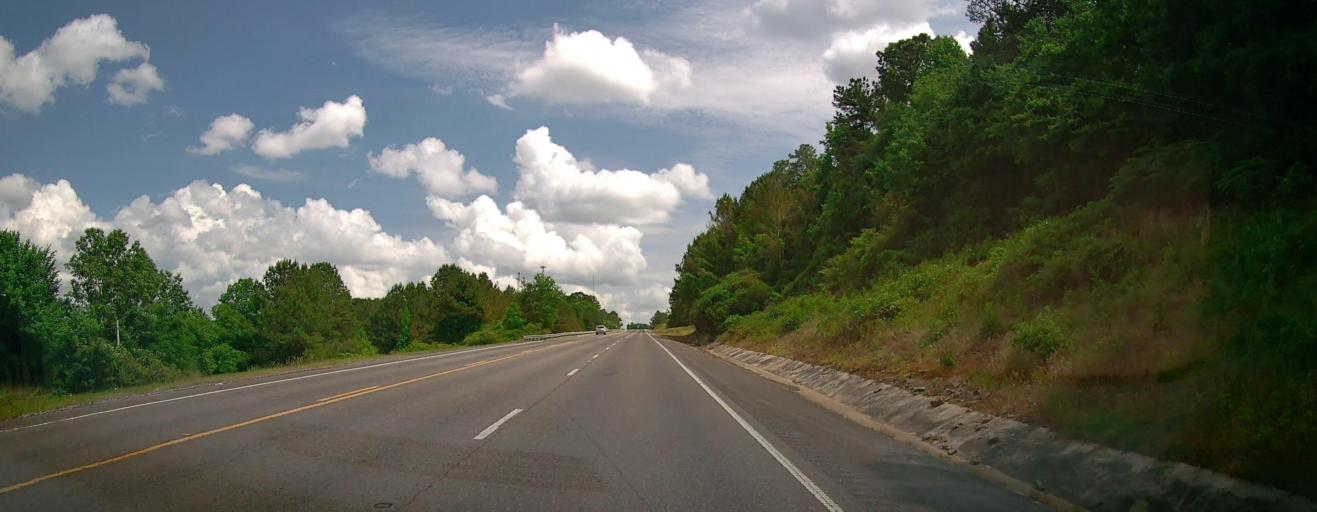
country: US
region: Alabama
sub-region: Marion County
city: Hamilton
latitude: 34.0884
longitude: -87.9816
